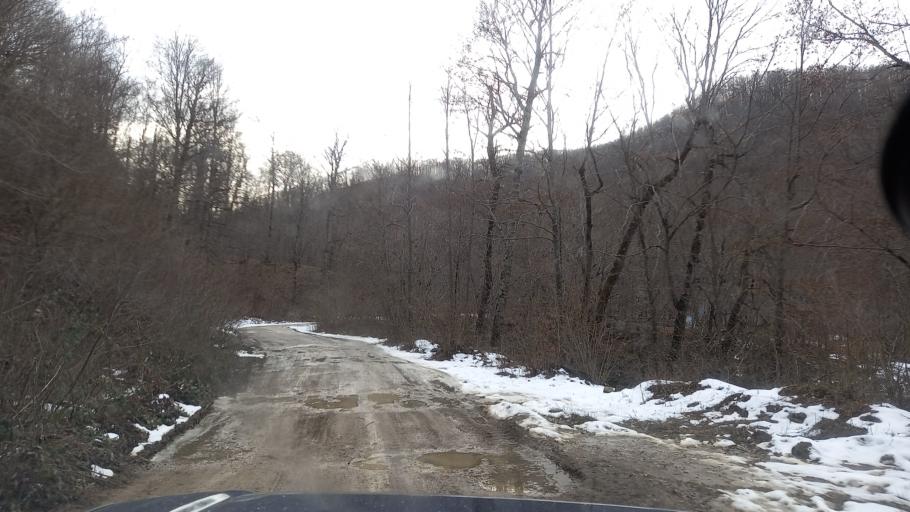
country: RU
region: Adygeya
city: Kamennomostskiy
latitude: 44.1633
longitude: 40.2987
